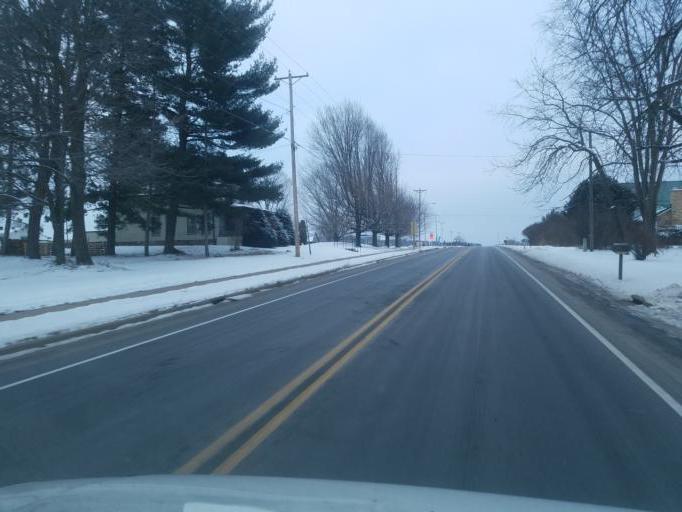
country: US
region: Wisconsin
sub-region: Waupaca County
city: Manawa
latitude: 44.4126
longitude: -88.8613
